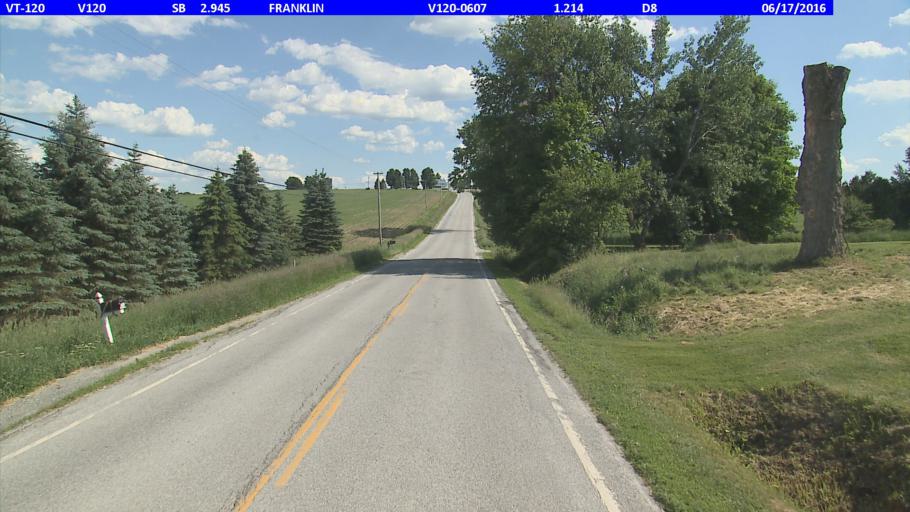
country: US
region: Vermont
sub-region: Franklin County
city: Enosburg Falls
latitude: 44.9505
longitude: -72.9051
